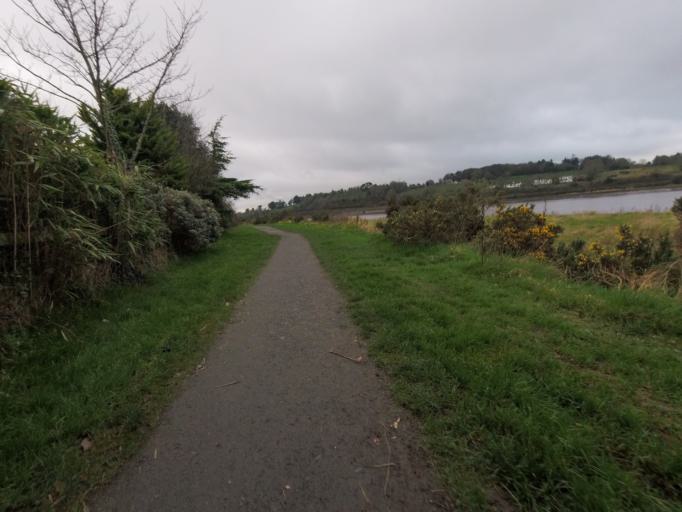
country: IE
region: Munster
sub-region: Waterford
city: Waterford
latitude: 52.2547
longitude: -7.0702
